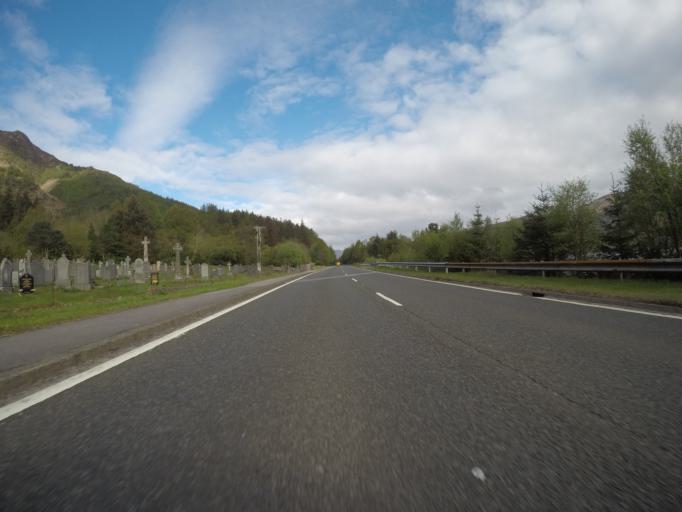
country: GB
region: Scotland
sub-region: Highland
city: Fort William
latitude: 56.6783
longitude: -5.1555
